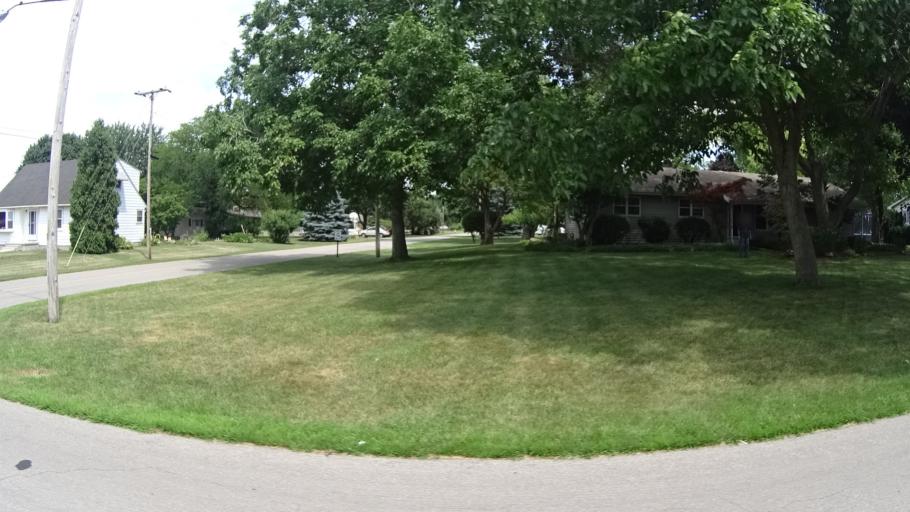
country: US
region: Ohio
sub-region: Erie County
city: Sandusky
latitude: 41.3970
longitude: -82.7845
